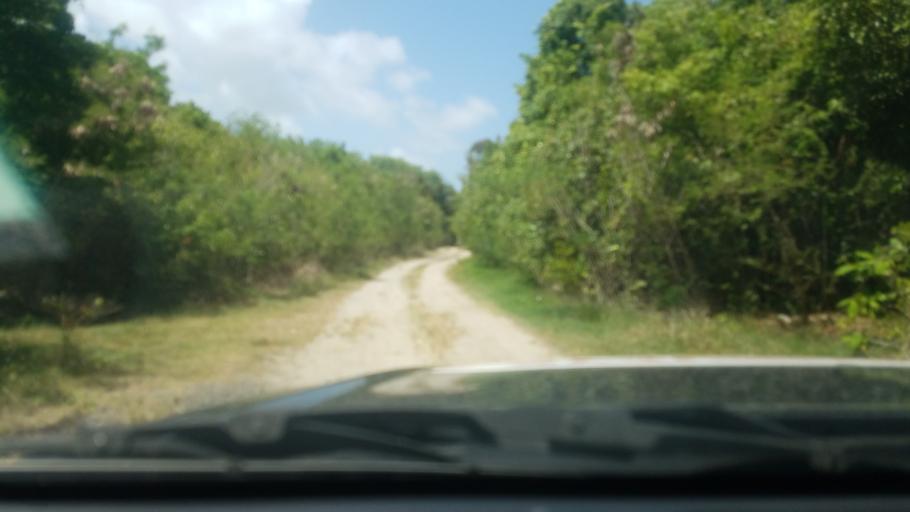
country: LC
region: Vieux-Fort
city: Vieux Fort
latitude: 13.7500
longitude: -60.9418
